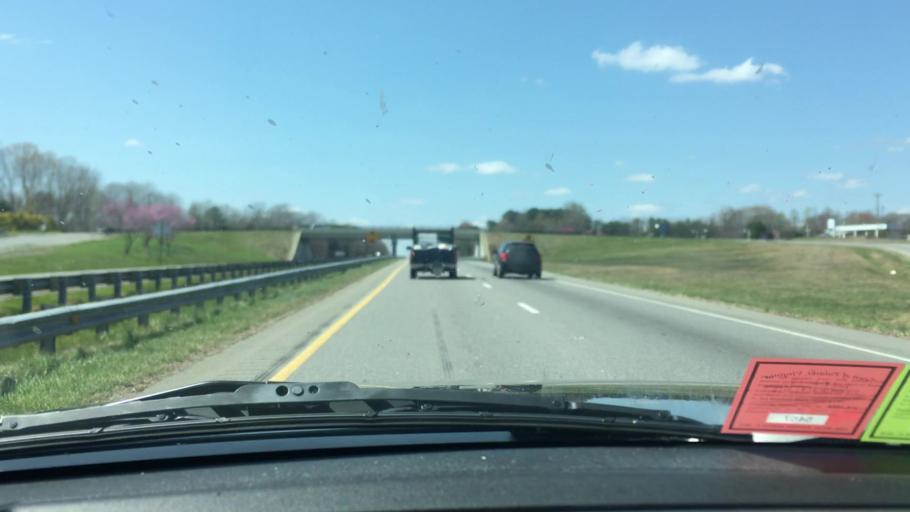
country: US
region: North Carolina
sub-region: Surry County
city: Pilot Mountain
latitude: 36.4064
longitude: -80.4979
